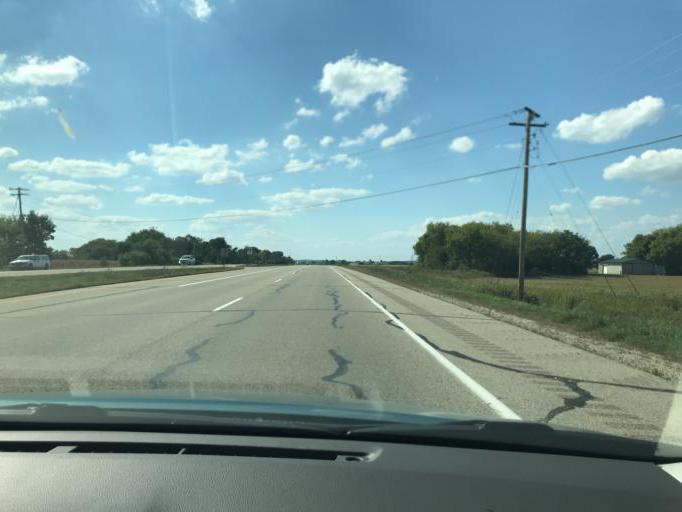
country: US
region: Wisconsin
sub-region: Walworth County
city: Pell Lake
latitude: 42.5966
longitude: -88.3584
